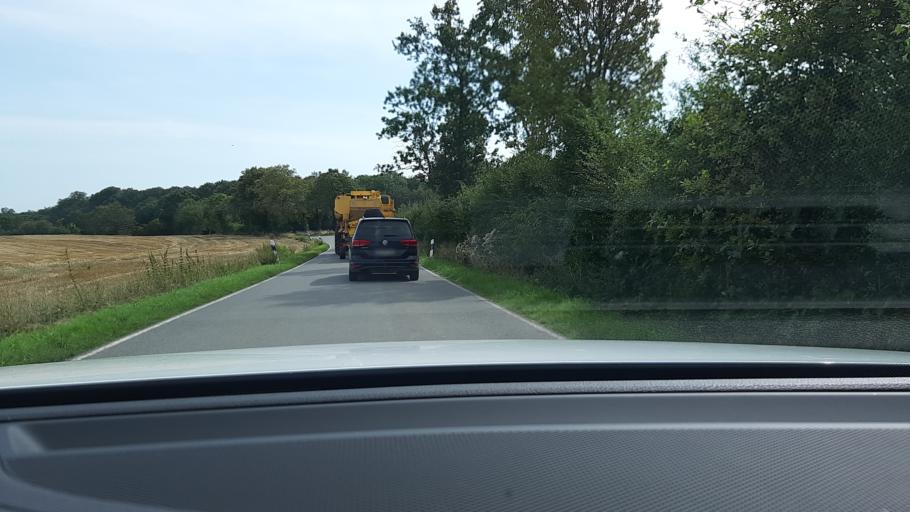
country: DE
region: Schleswig-Holstein
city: Rehhorst
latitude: 53.8600
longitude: 10.4640
